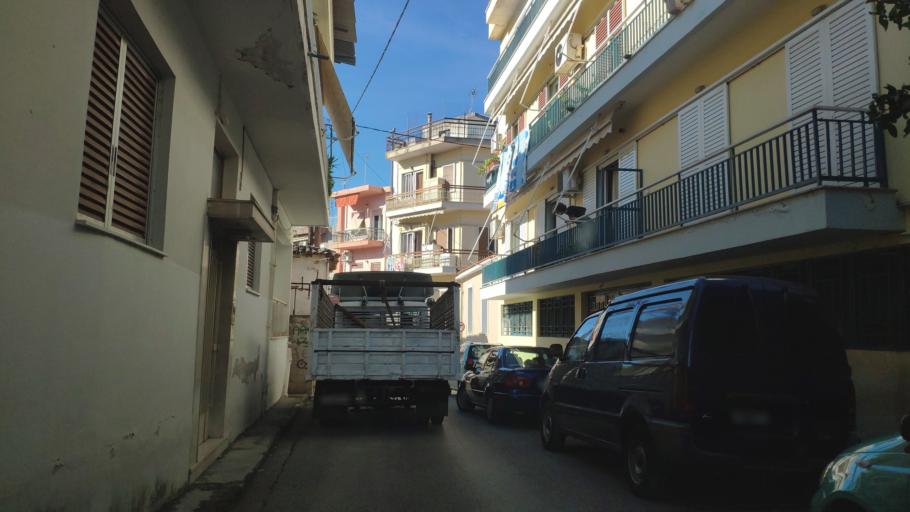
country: GR
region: Central Greece
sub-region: Nomos Voiotias
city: Livadeia
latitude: 38.4356
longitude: 22.8768
